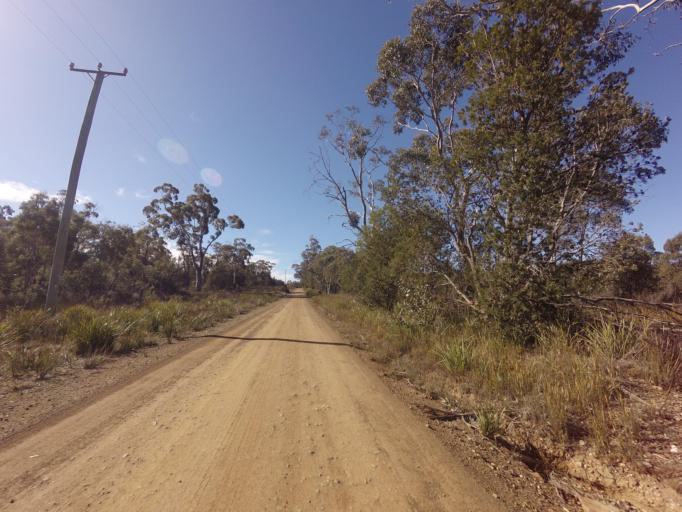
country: AU
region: Tasmania
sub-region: Sorell
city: Sorell
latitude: -42.3564
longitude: 147.9645
